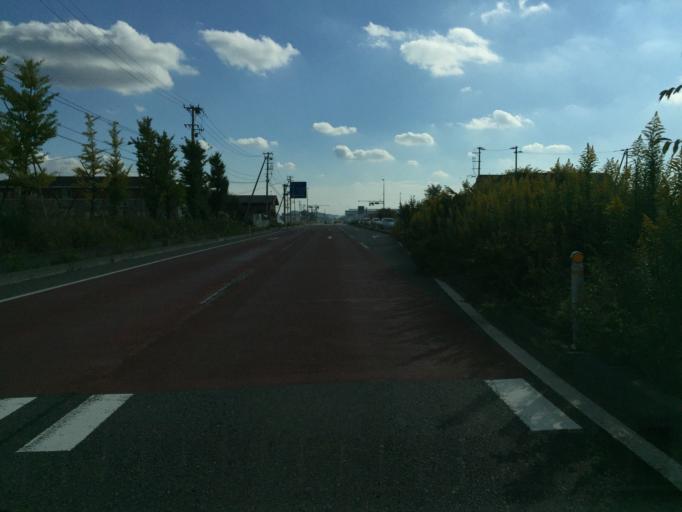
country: JP
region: Fukushima
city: Motomiya
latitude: 37.5408
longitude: 140.3972
